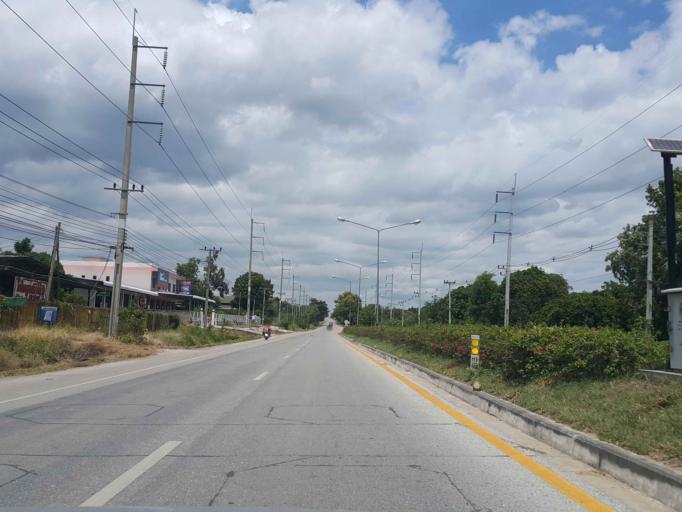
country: TH
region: Lamphun
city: Ban Hong
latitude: 18.3599
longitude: 98.8107
